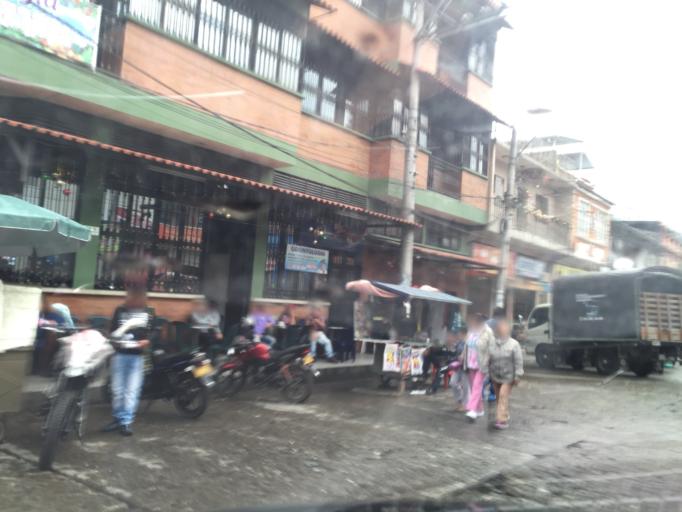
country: CO
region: Tolima
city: Cajamarca
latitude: 4.4416
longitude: -75.4272
